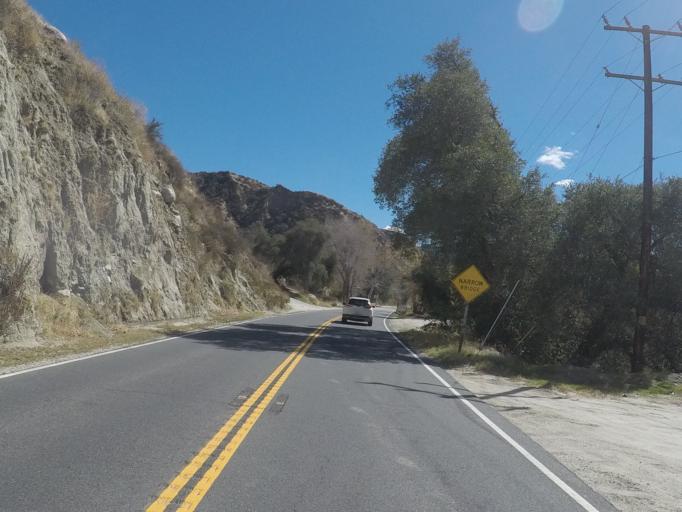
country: US
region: California
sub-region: Riverside County
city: Valle Vista
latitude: 33.7318
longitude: -116.8107
